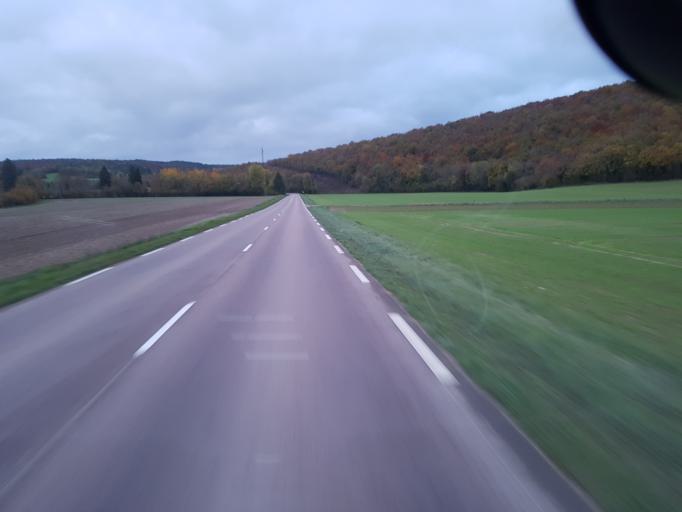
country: FR
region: Champagne-Ardenne
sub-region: Departement de l'Aube
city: Mussy-sur-Seine
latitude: 48.0061
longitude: 4.4743
